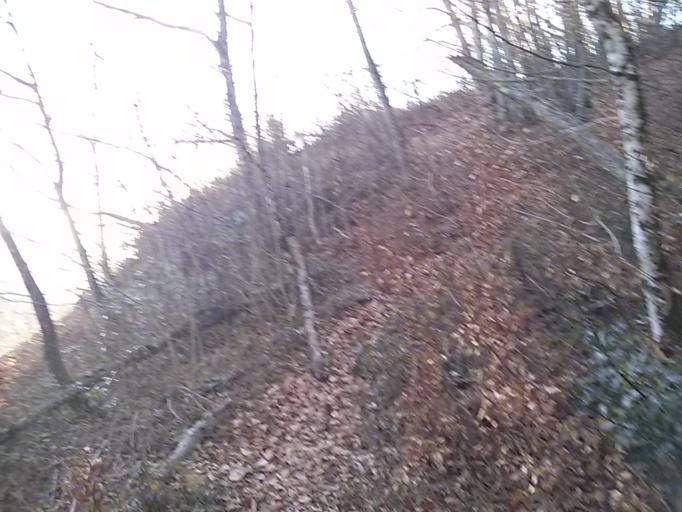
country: FR
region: Rhone-Alpes
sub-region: Departement de la Savoie
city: Chatillon
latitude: 45.7997
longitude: 5.8752
